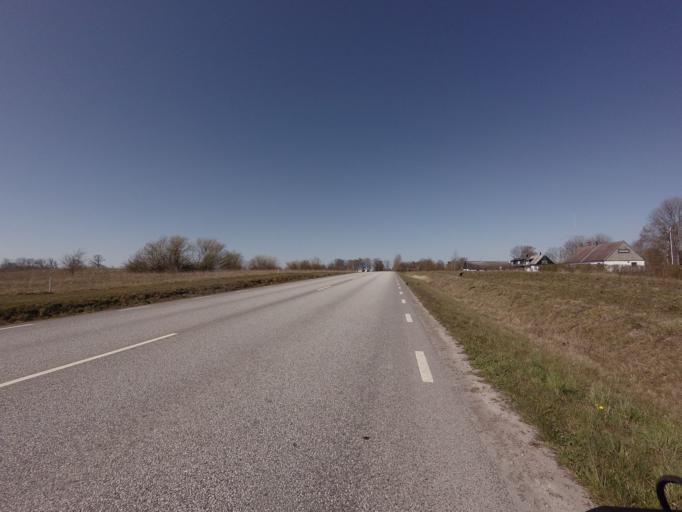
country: SE
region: Skane
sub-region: Vellinge Kommun
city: Vellinge
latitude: 55.4668
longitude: 13.0750
